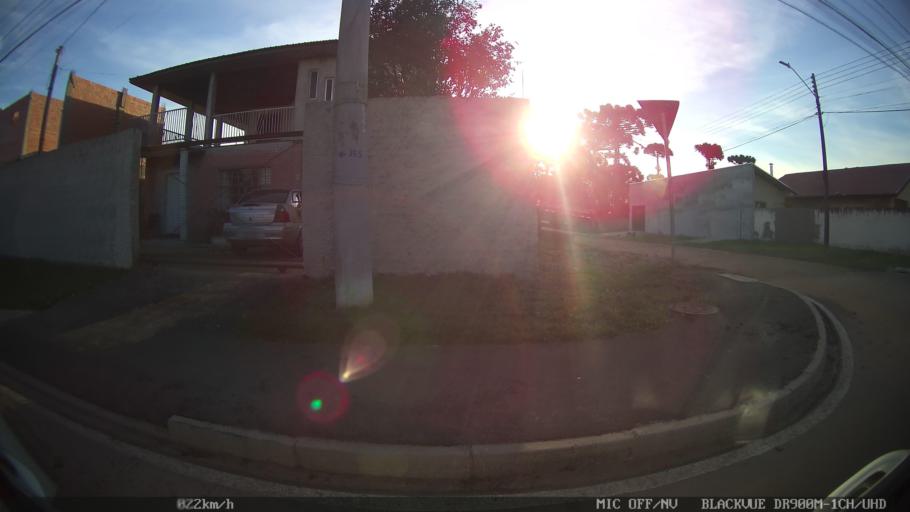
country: BR
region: Parana
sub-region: Pinhais
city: Pinhais
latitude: -25.4611
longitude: -49.1511
